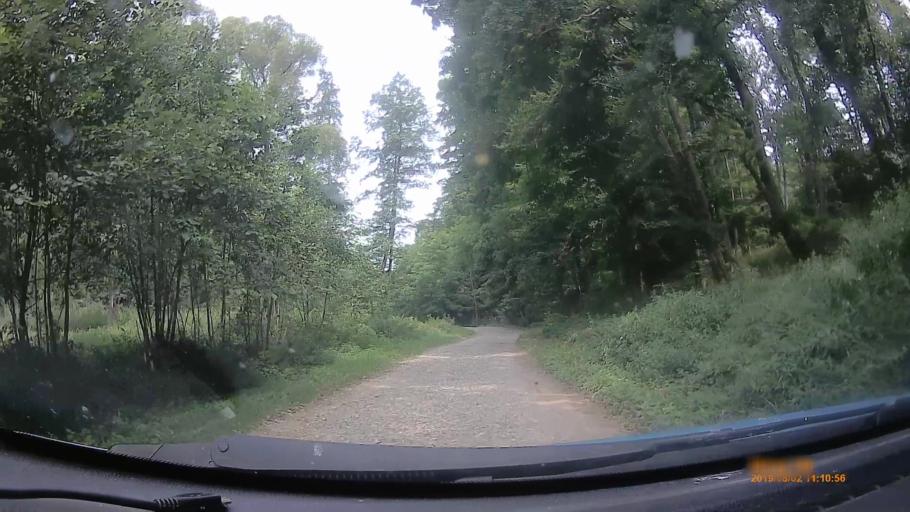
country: HU
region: Baranya
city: Buekkoesd
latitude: 46.1059
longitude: 17.9366
